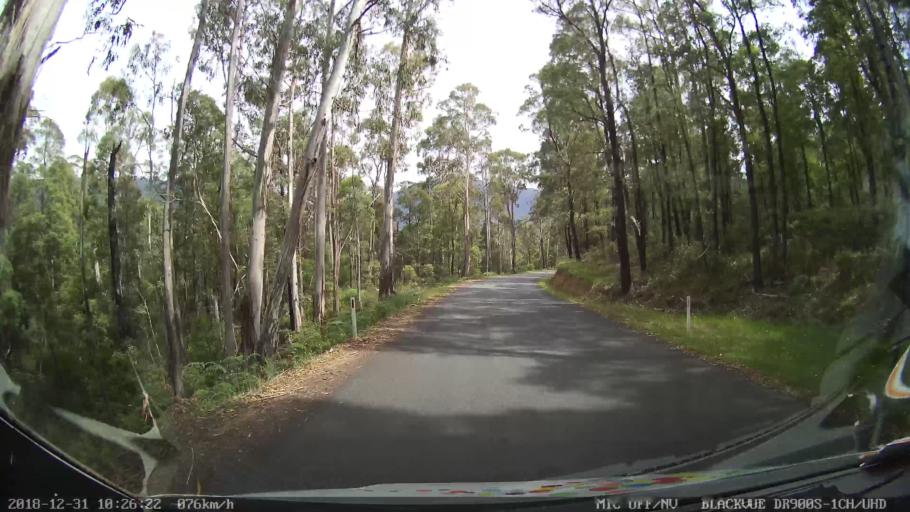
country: AU
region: New South Wales
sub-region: Snowy River
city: Jindabyne
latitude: -36.4965
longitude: 148.1401
